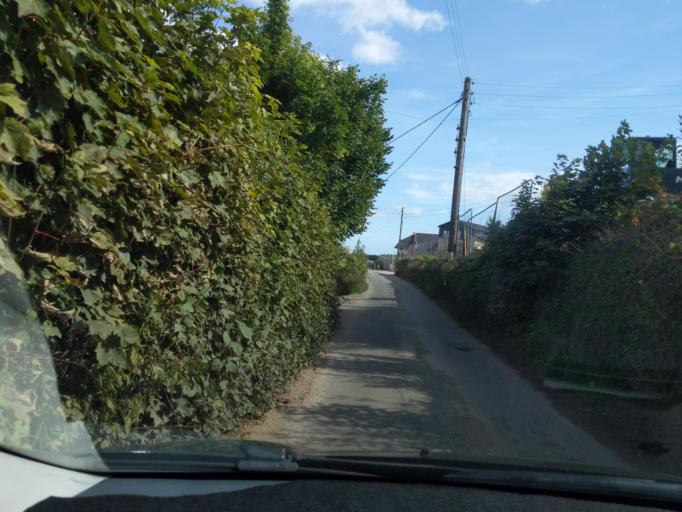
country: GB
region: England
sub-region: Devon
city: Marldon
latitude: 50.4603
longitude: -3.6009
